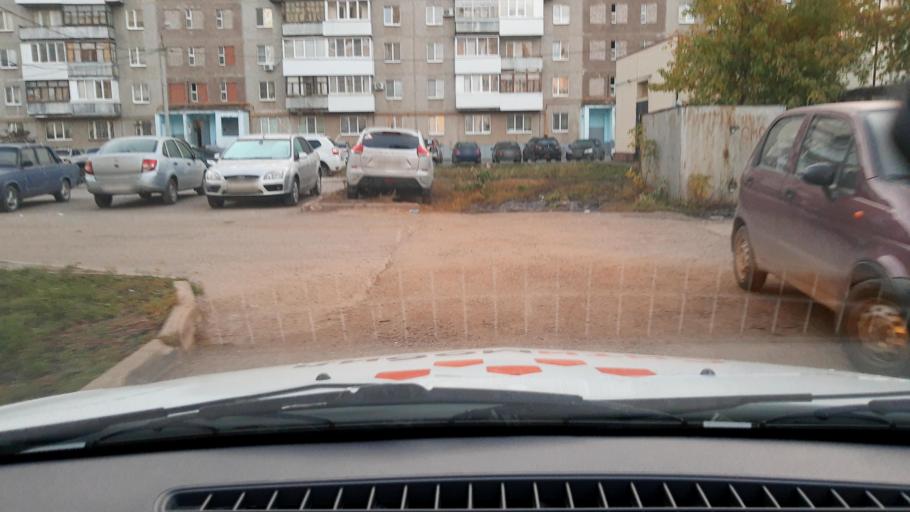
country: RU
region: Bashkortostan
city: Iglino
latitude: 54.7695
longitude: 56.2284
